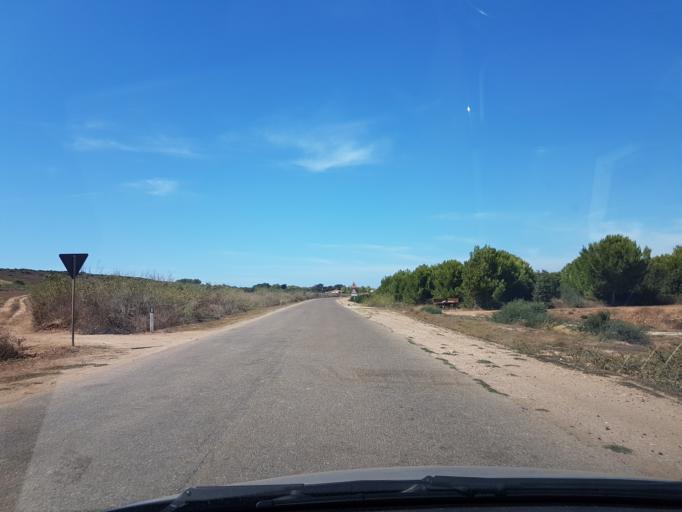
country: IT
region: Sardinia
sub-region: Provincia di Oristano
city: Cabras
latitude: 39.9516
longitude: 8.4552
